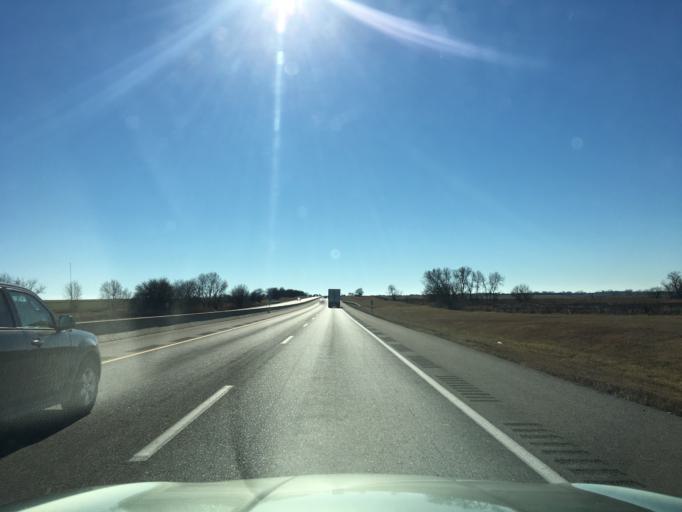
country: US
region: Kansas
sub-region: Sumner County
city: Wellington
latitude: 37.1154
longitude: -97.3389
